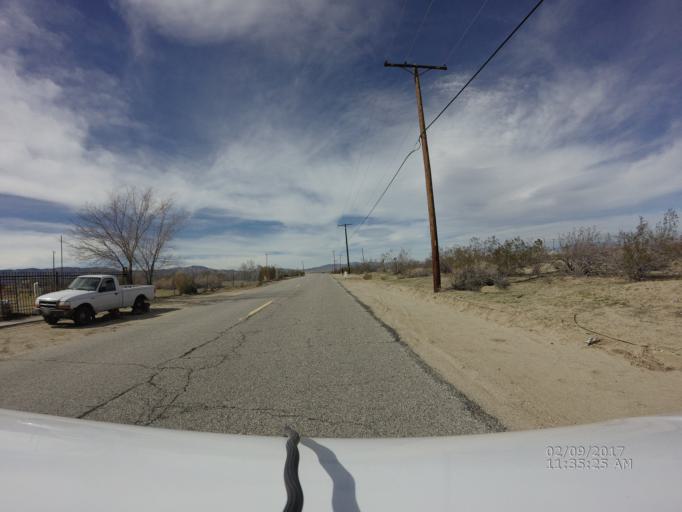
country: US
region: California
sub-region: Los Angeles County
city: Littlerock
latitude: 34.5211
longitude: -117.9355
